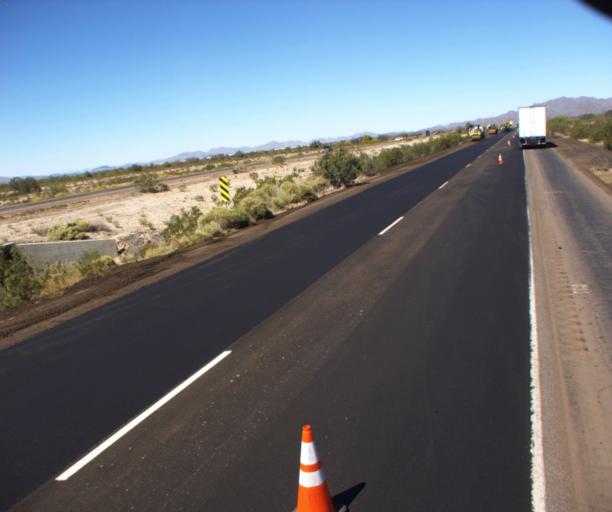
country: US
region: Arizona
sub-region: Maricopa County
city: Gila Bend
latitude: 33.0356
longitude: -112.6461
